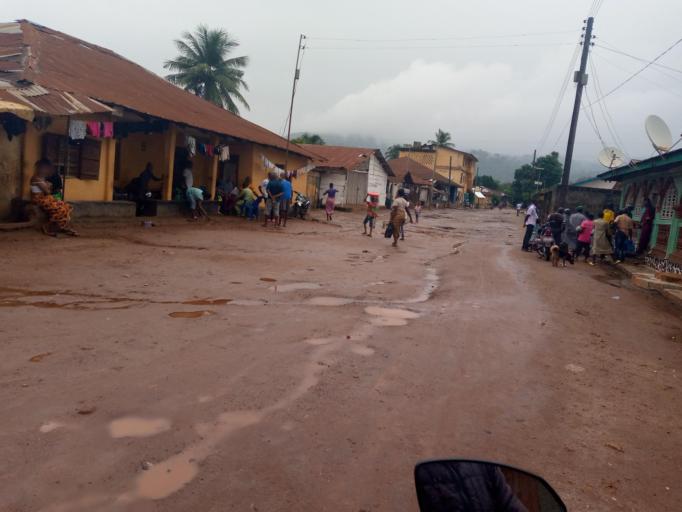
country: SL
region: Eastern Province
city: Kenema
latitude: 7.8805
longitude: -11.1858
